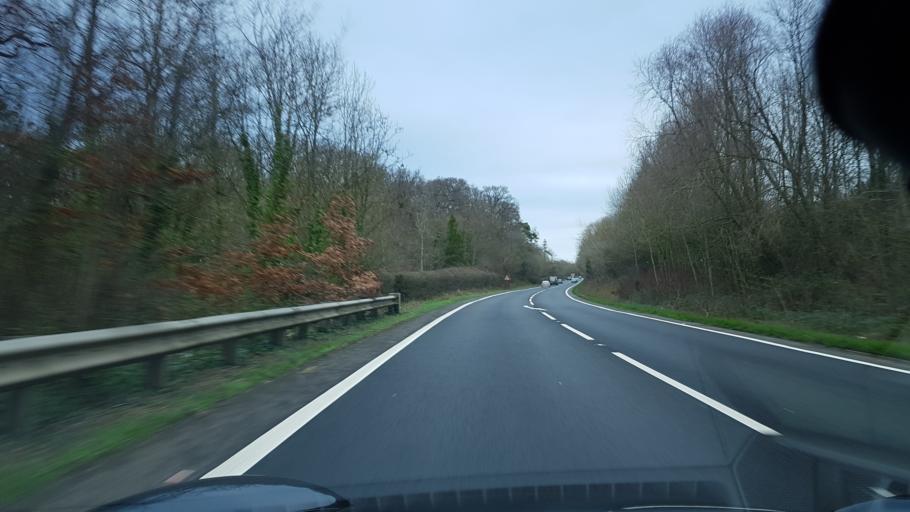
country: GB
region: England
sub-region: Somerset
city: Creech Saint Michael
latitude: 50.9783
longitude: -3.0090
